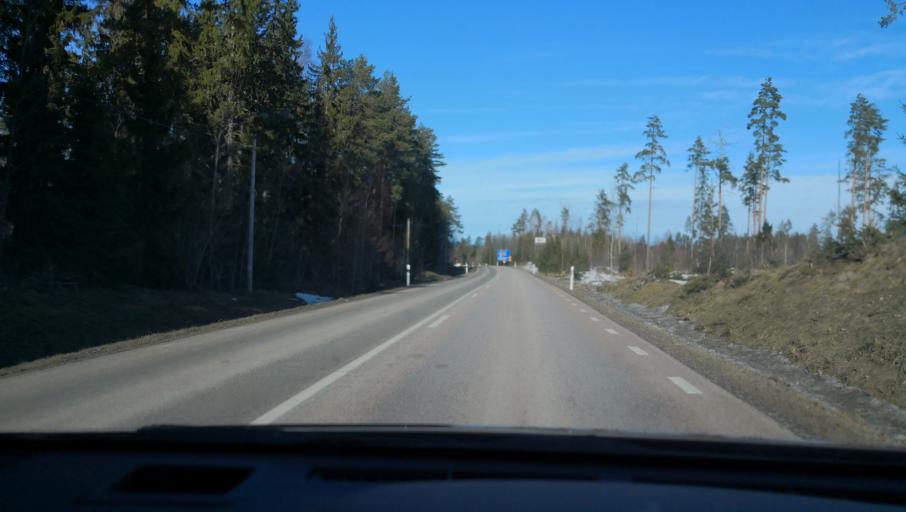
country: SE
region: Uppsala
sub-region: Osthammars Kommun
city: Osterbybruk
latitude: 60.1908
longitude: 17.8772
